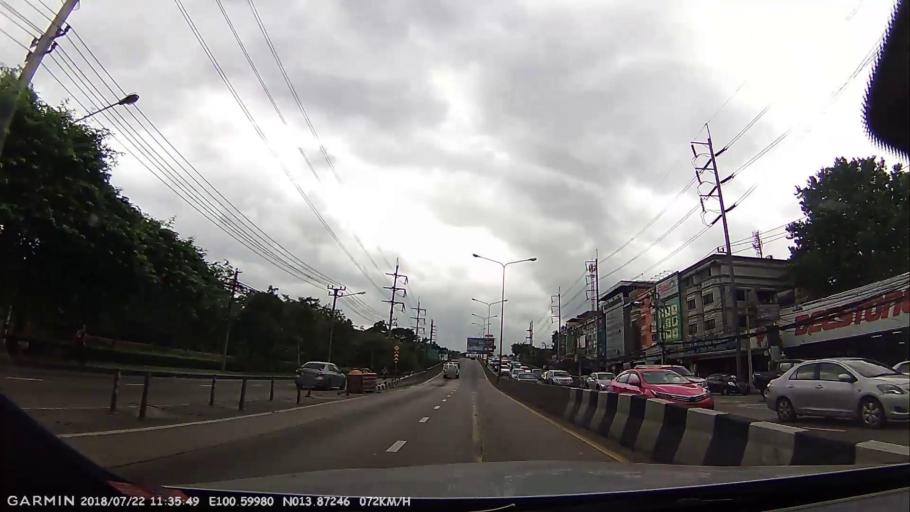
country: TH
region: Bangkok
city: Lak Si
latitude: 13.8725
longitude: 100.5997
